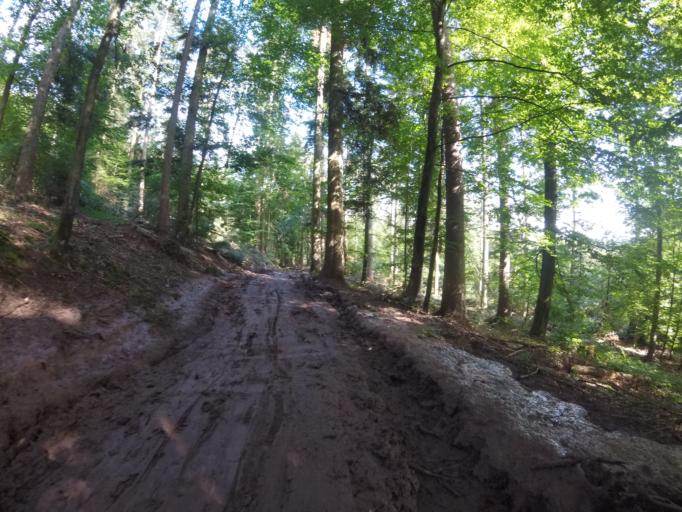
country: DE
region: Baden-Wuerttemberg
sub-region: Regierungsbezirk Stuttgart
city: Sulzbach an der Murr
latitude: 48.9697
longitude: 9.5248
